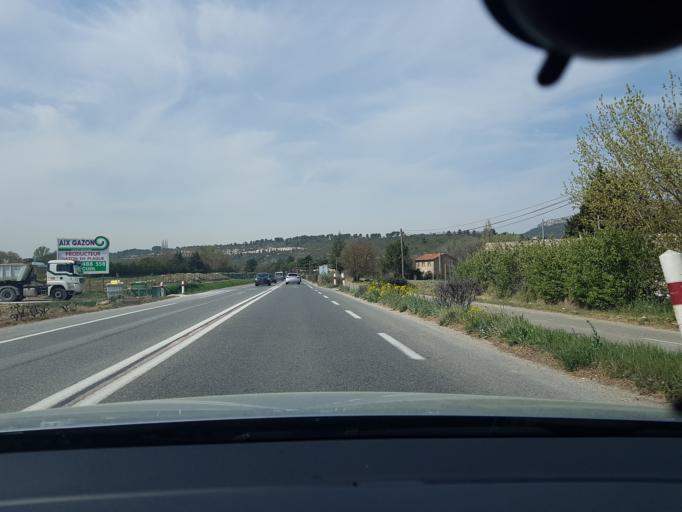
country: FR
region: Provence-Alpes-Cote d'Azur
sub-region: Departement des Bouches-du-Rhone
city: Chateauneuf-le-Rouge
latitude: 43.4760
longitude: 5.5735
